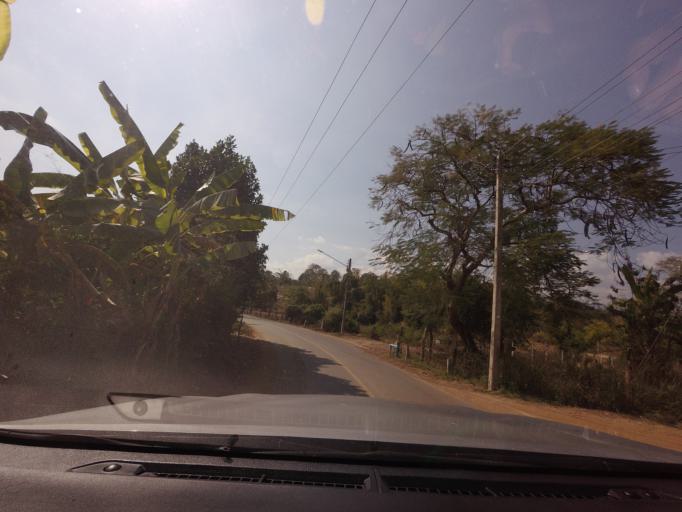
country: TH
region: Mae Hong Son
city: Wiang Nuea
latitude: 19.4013
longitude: 98.4426
